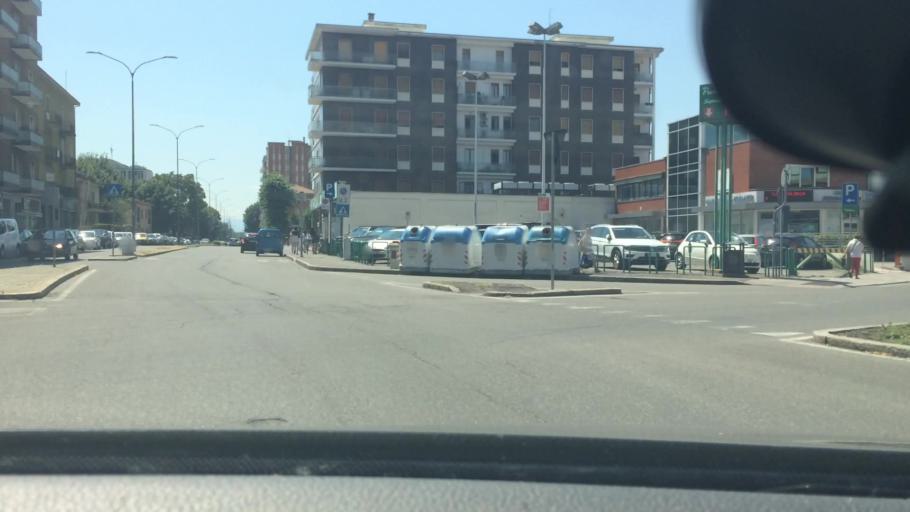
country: IT
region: Emilia-Romagna
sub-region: Provincia di Piacenza
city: Piacenza
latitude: 45.0450
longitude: 9.6832
